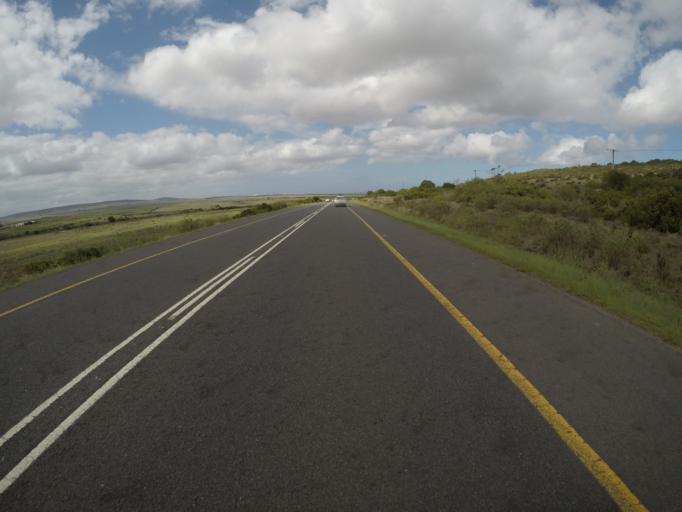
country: ZA
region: Western Cape
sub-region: Eden District Municipality
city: Mossel Bay
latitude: -34.1775
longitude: 21.9074
